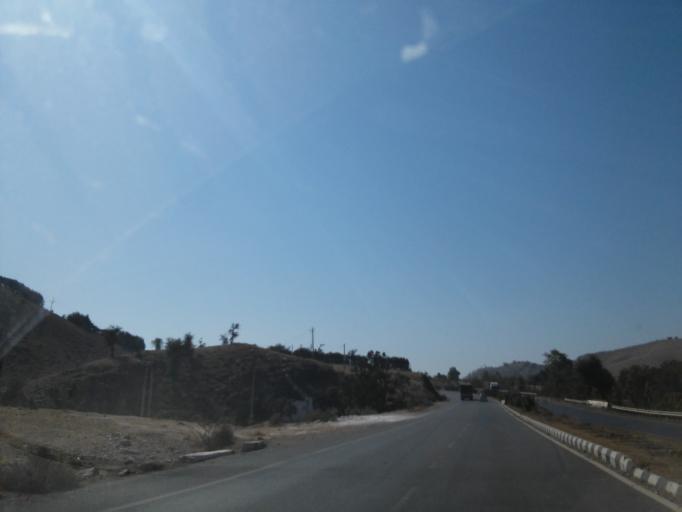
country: IN
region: Rajasthan
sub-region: Dungarpur
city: Dungarpur
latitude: 24.0163
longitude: 73.6579
